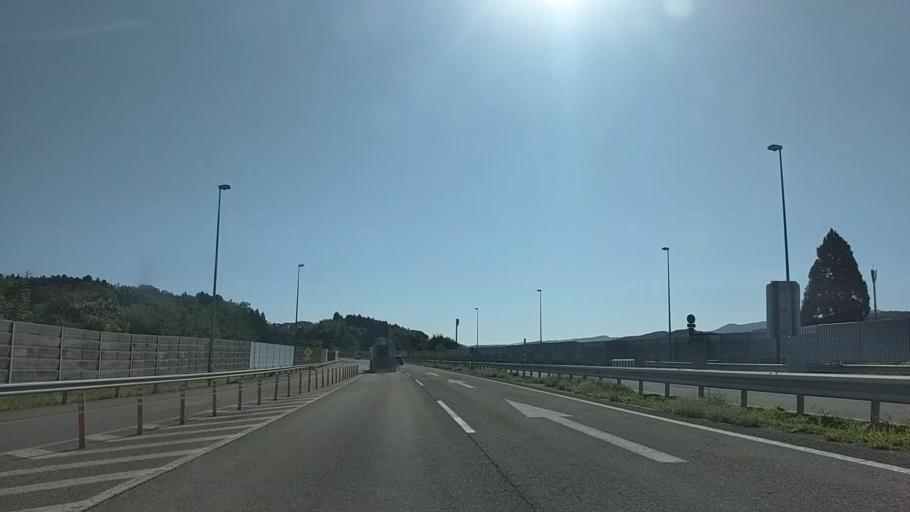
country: JP
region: Ishikawa
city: Tsubata
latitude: 36.6067
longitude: 136.7076
